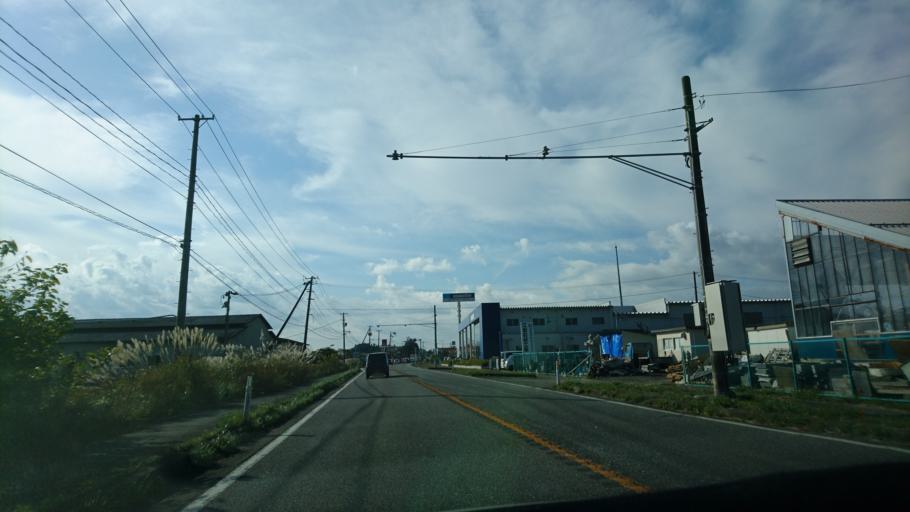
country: JP
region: Miyagi
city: Furukawa
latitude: 38.6101
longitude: 140.9830
